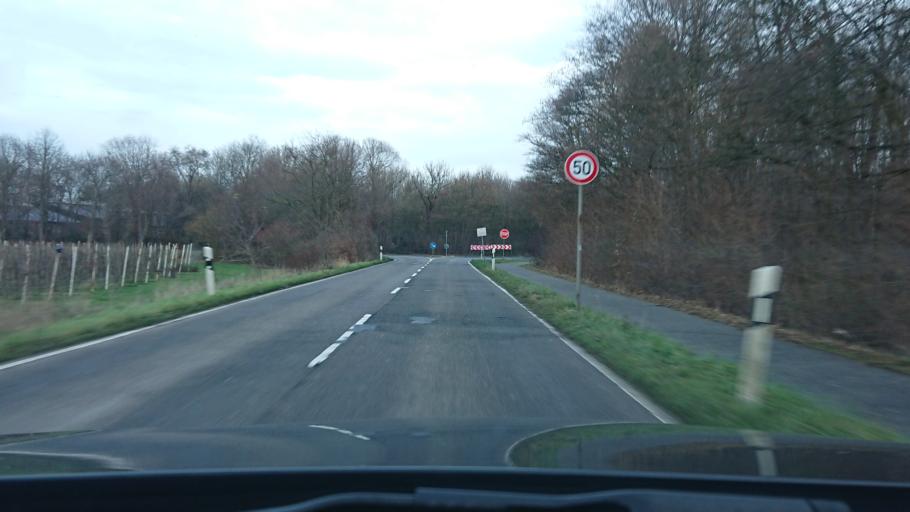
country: DE
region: North Rhine-Westphalia
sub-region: Regierungsbezirk Koln
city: Pulheim
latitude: 51.0268
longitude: 6.7801
